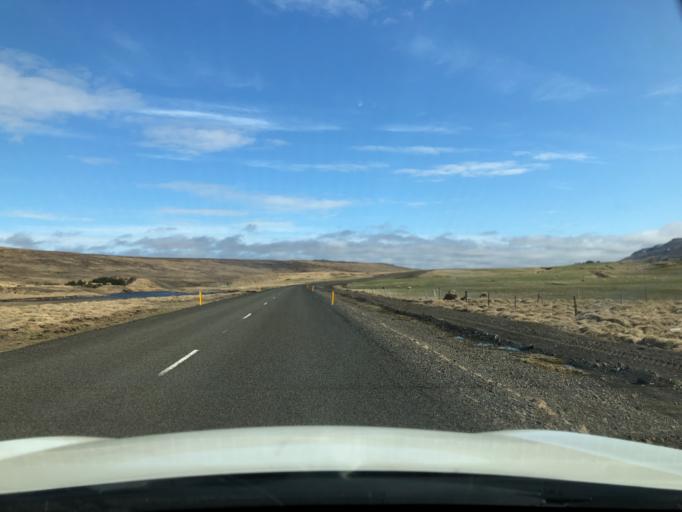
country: IS
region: West
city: Borgarnes
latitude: 65.1425
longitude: -21.5910
